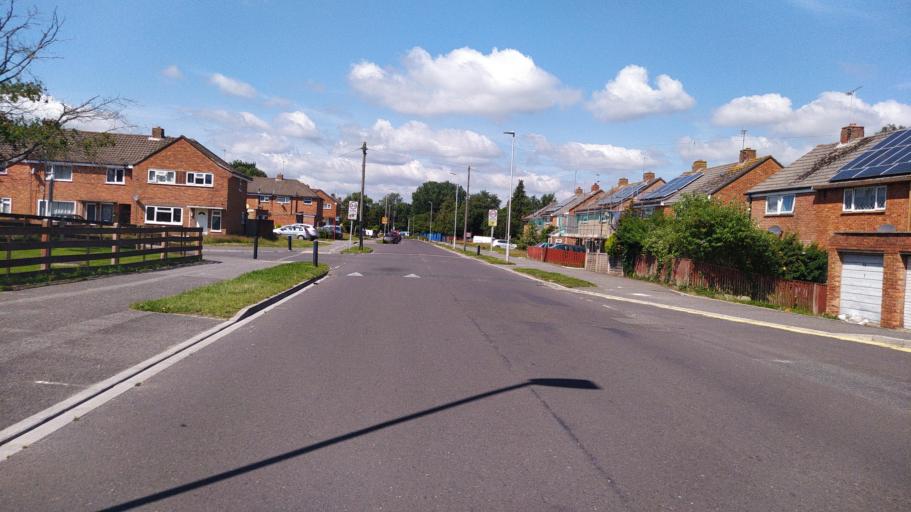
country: GB
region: England
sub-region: Poole
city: Poole
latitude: 50.7256
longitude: -2.0229
